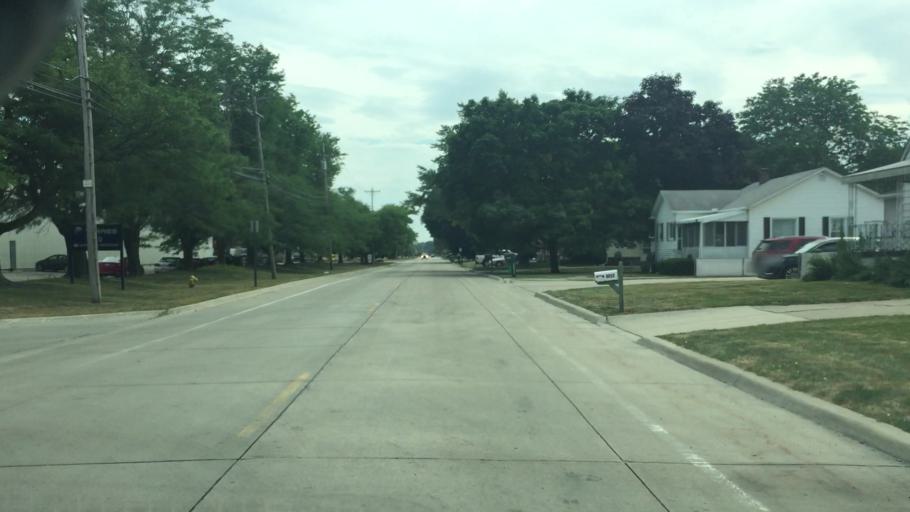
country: US
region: Michigan
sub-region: Monroe County
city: Monroe
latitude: 41.9231
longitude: -83.3680
